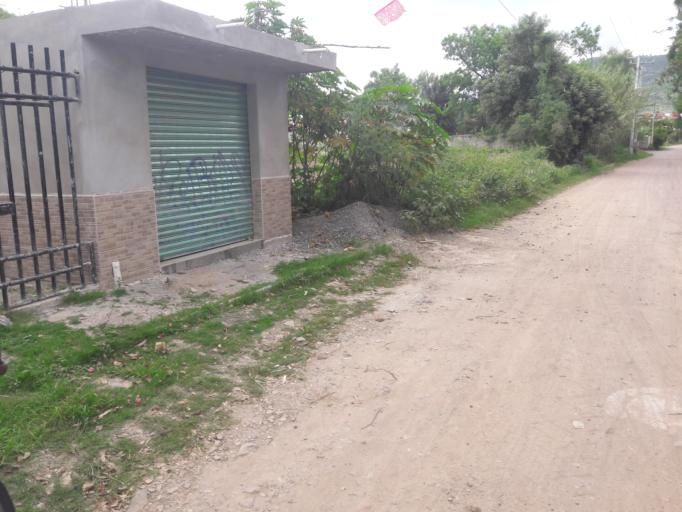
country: MX
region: Oaxaca
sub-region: Heroica Ciudad de Huajuapan de Leon
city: La Junta
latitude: 17.8279
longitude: -97.7460
